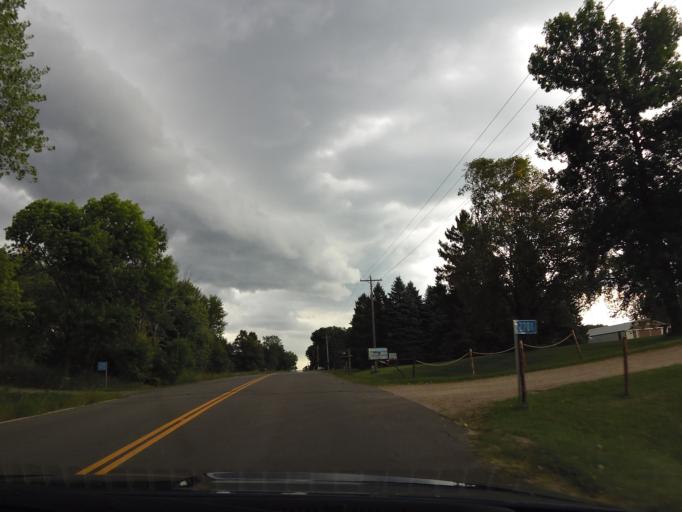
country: US
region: Minnesota
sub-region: Scott County
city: Prior Lake
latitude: 44.6886
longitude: -93.4679
